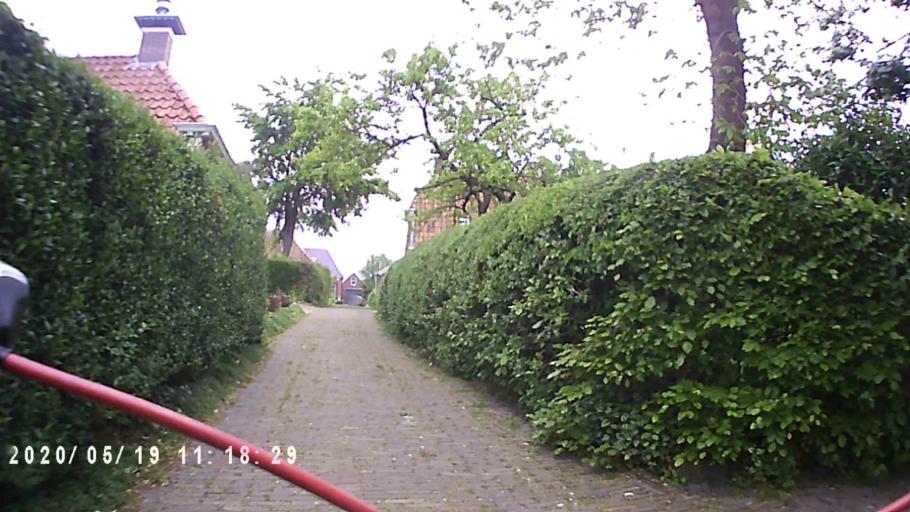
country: NL
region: Groningen
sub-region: Gemeente Zuidhorn
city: Oldehove
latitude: 53.2907
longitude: 6.3673
